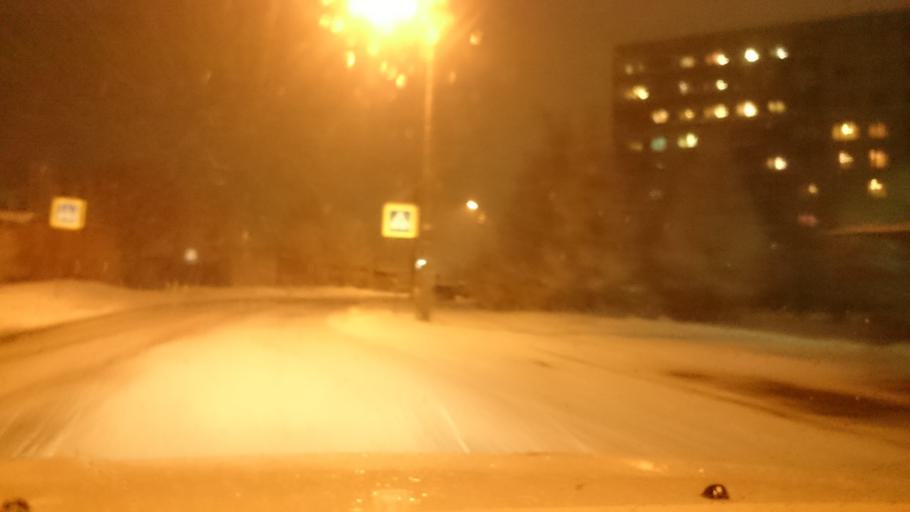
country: RU
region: Tula
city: Mendeleyevskiy
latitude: 54.1645
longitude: 37.5616
